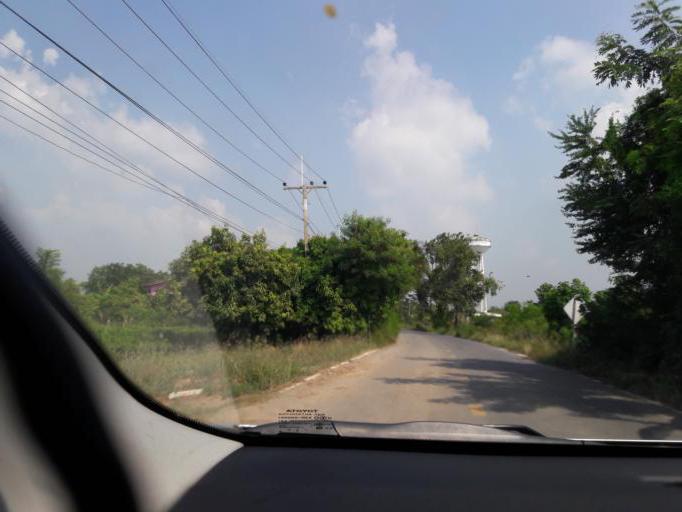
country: TH
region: Ang Thong
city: Ang Thong
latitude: 14.5434
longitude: 100.4161
